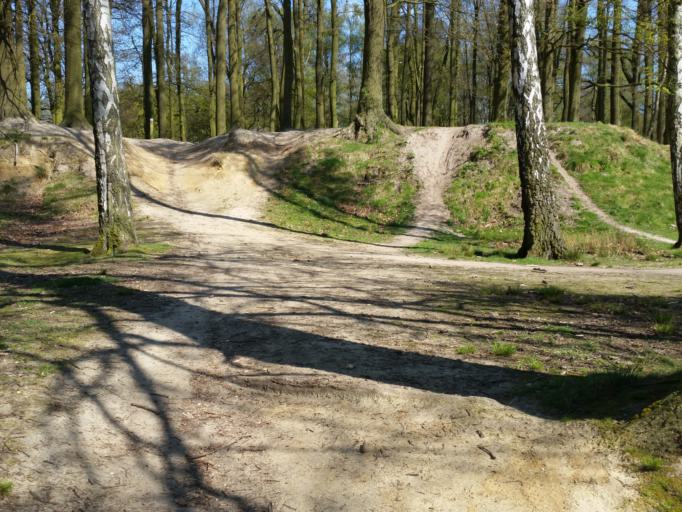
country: BE
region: Flanders
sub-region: Provincie Antwerpen
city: Bonheiden
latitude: 50.9886
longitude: 4.5116
